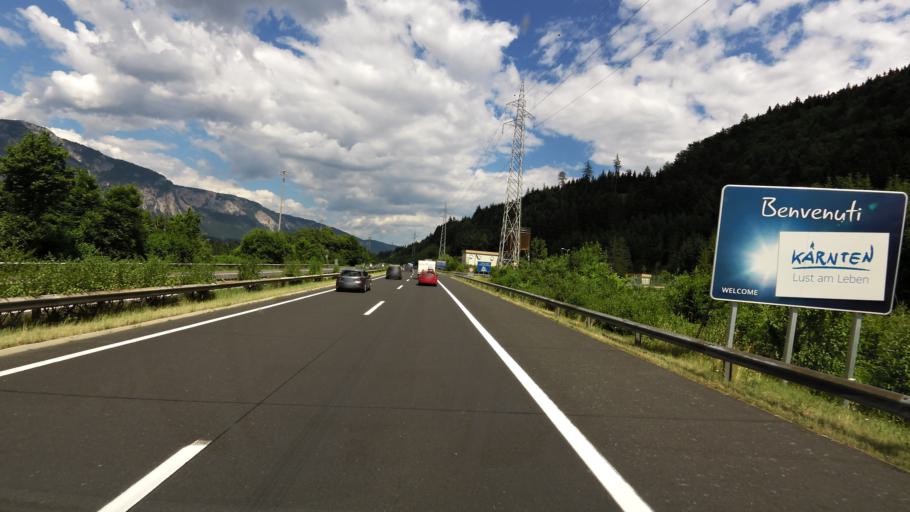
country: AT
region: Carinthia
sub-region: Politischer Bezirk Villach Land
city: Hohenthurn
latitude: 46.5385
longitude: 13.6660
